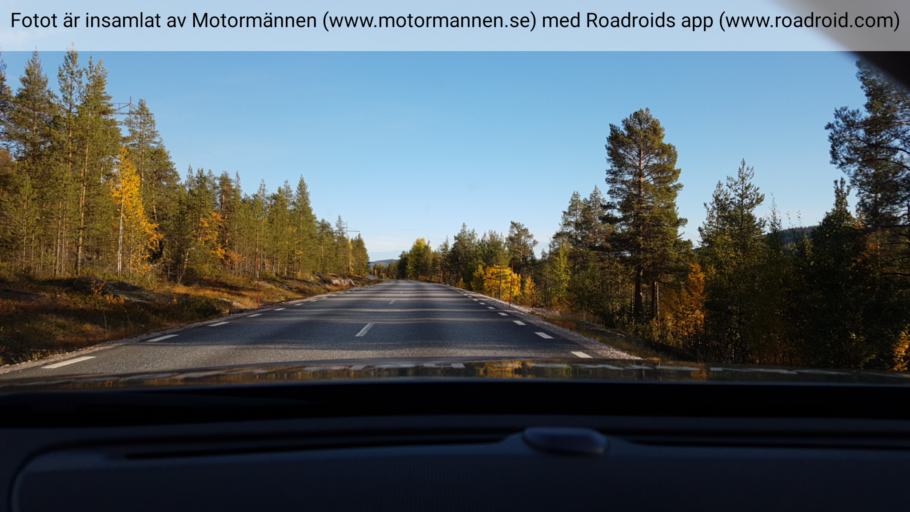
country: SE
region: Norrbotten
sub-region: Jokkmokks Kommun
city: Jokkmokk
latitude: 66.8351
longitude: 19.8474
